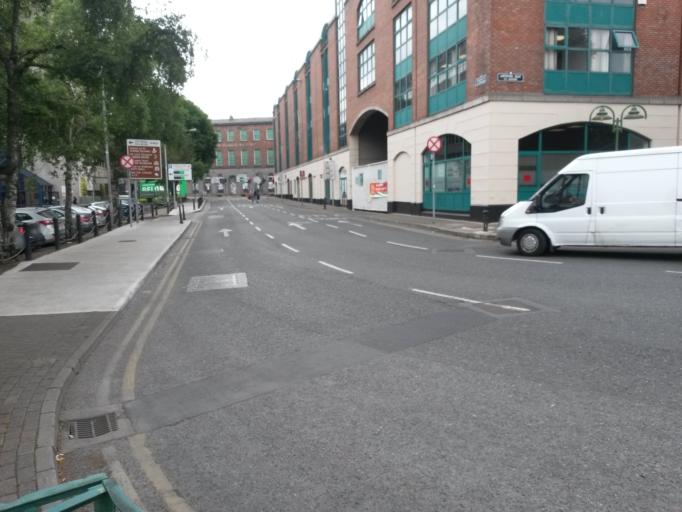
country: IE
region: Munster
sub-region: County Limerick
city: Luimneach
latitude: 52.6660
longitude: -8.6260
